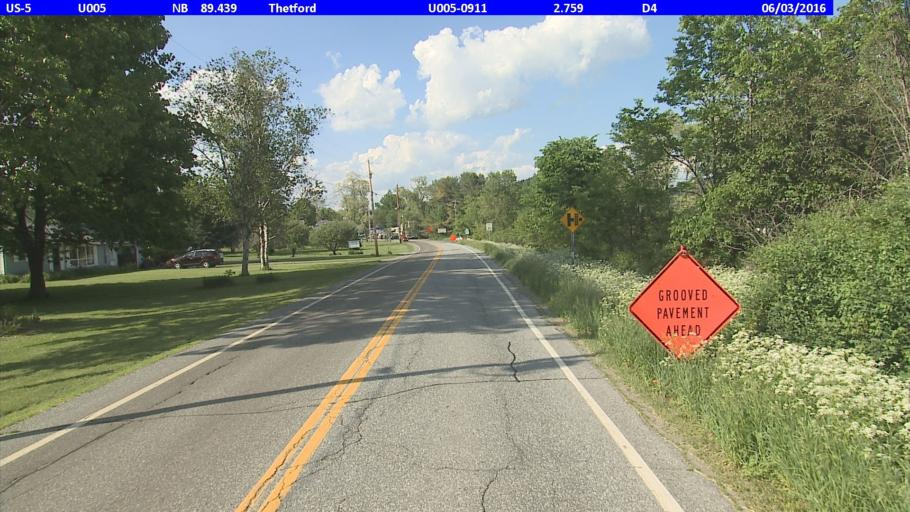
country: US
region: New Hampshire
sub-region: Grafton County
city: Lyme
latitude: 43.8083
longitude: -72.1895
